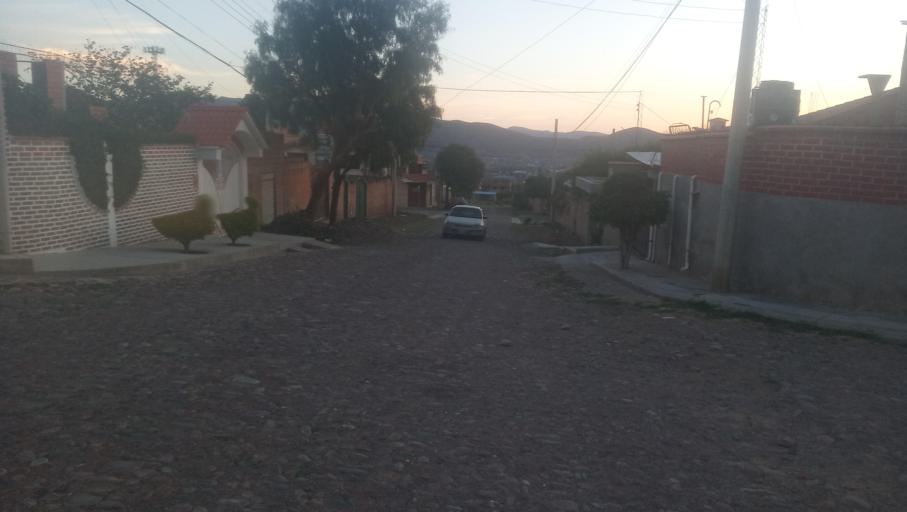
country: BO
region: Cochabamba
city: Cochabamba
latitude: -17.3738
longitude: -66.0940
